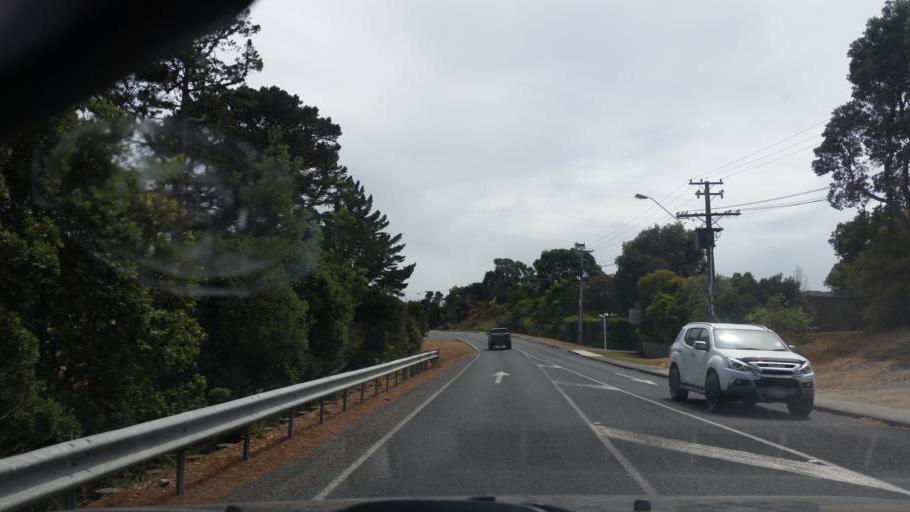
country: NZ
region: Auckland
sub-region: Auckland
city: Wellsford
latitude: -36.0953
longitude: 174.5860
